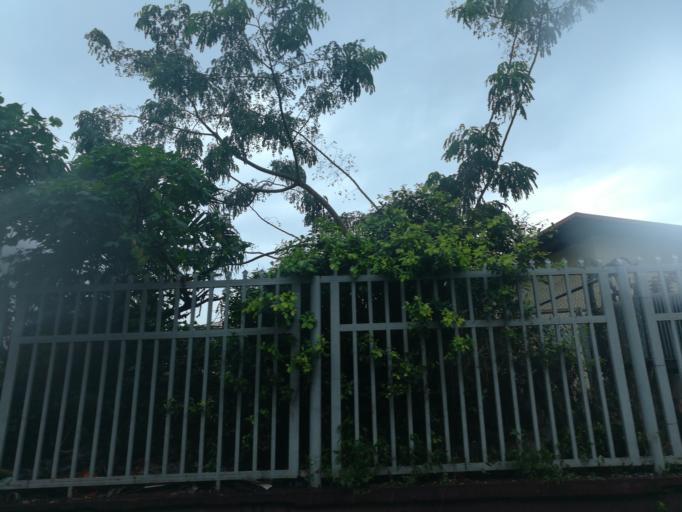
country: NG
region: Lagos
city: Lagos
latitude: 6.4494
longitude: 3.4025
